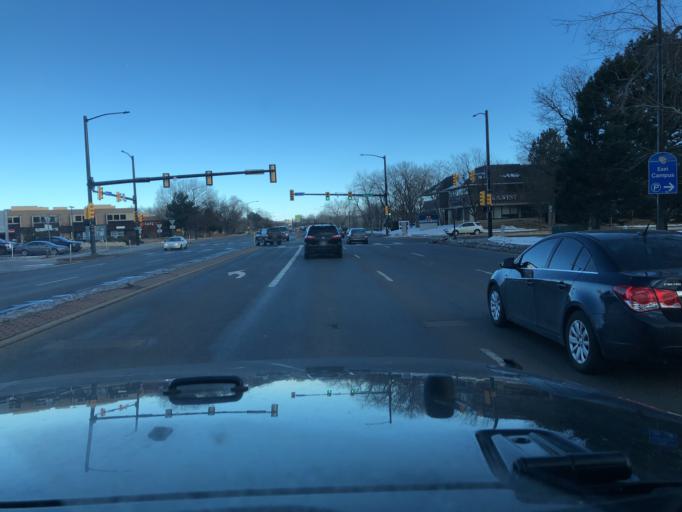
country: US
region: Colorado
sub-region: Boulder County
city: Boulder
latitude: 40.0146
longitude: -105.2476
